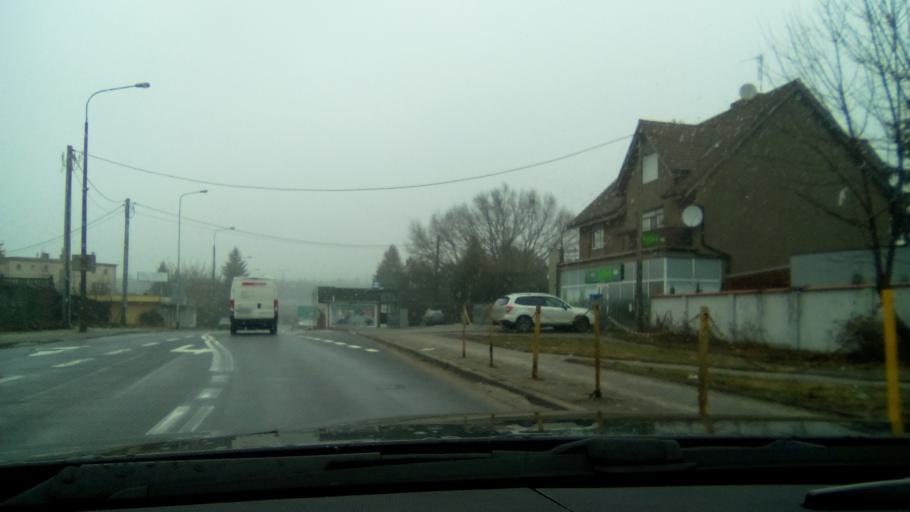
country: PL
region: Greater Poland Voivodeship
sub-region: Powiat poznanski
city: Swarzedz
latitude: 52.4084
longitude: 17.0250
